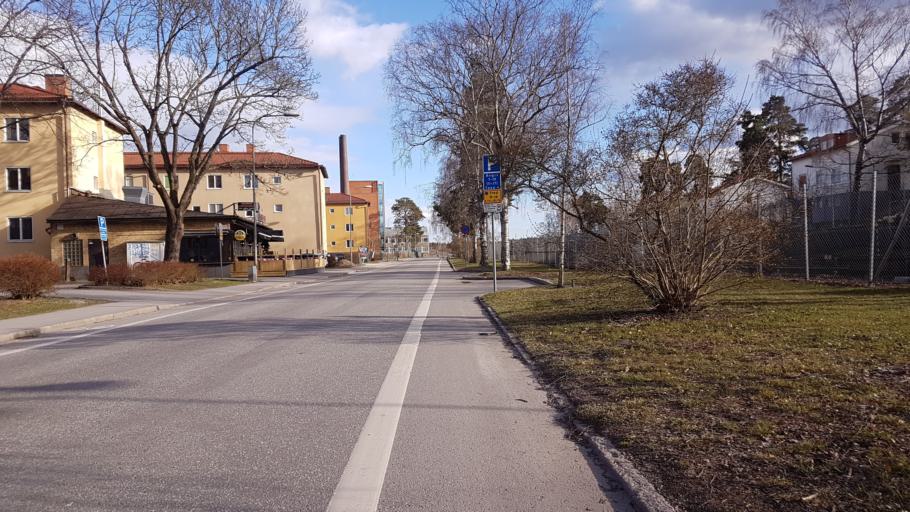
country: SE
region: Stockholm
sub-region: Stockholms Kommun
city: Arsta
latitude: 59.2883
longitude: 18.0715
